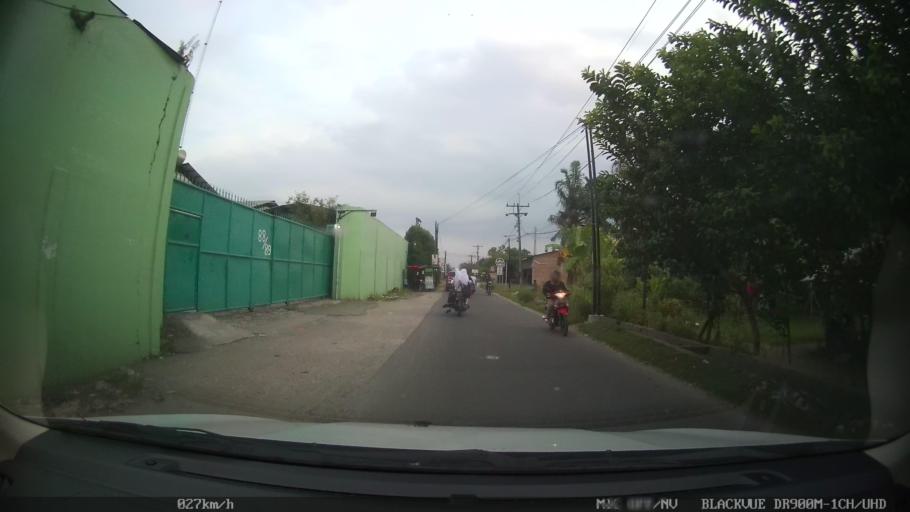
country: ID
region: North Sumatra
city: Sunggal
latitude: 3.5687
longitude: 98.6041
